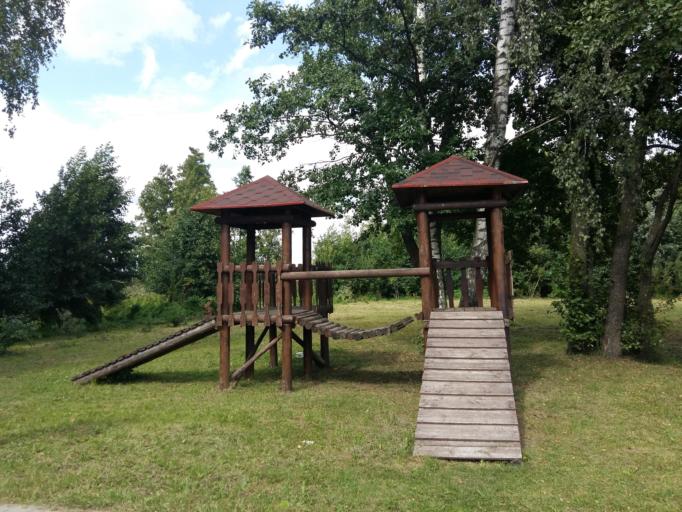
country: LT
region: Marijampoles apskritis
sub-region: Marijampole Municipality
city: Marijampole
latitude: 54.6584
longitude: 23.4003
